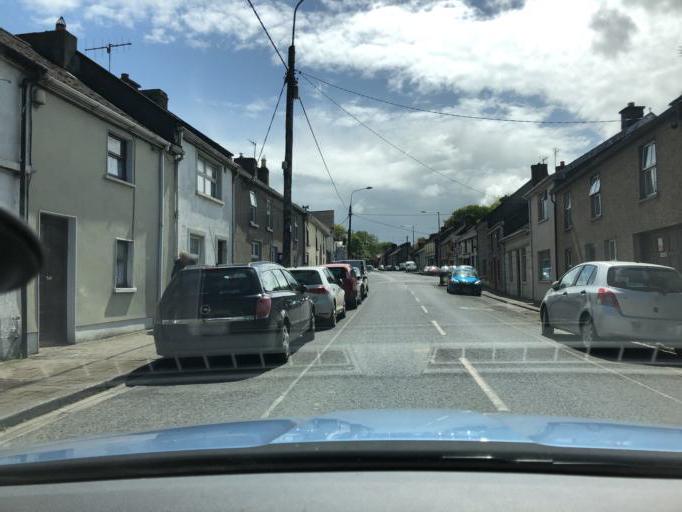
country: IE
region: Munster
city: Cashel
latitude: 52.5166
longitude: -7.8920
